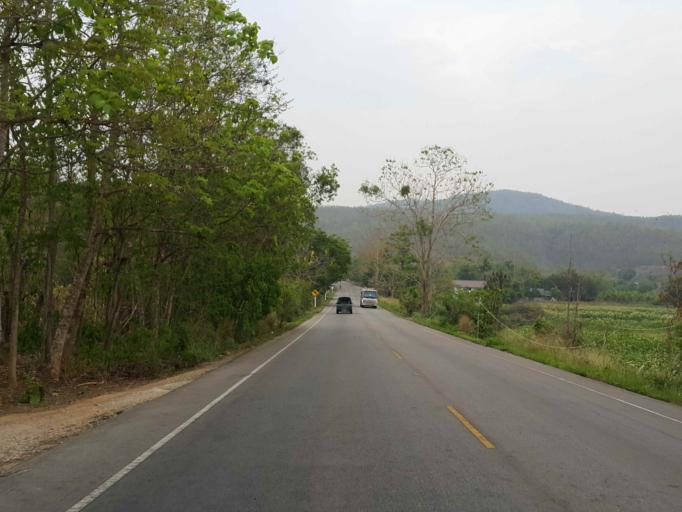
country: TH
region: Chiang Mai
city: Mae Taeng
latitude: 19.0891
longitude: 98.9951
